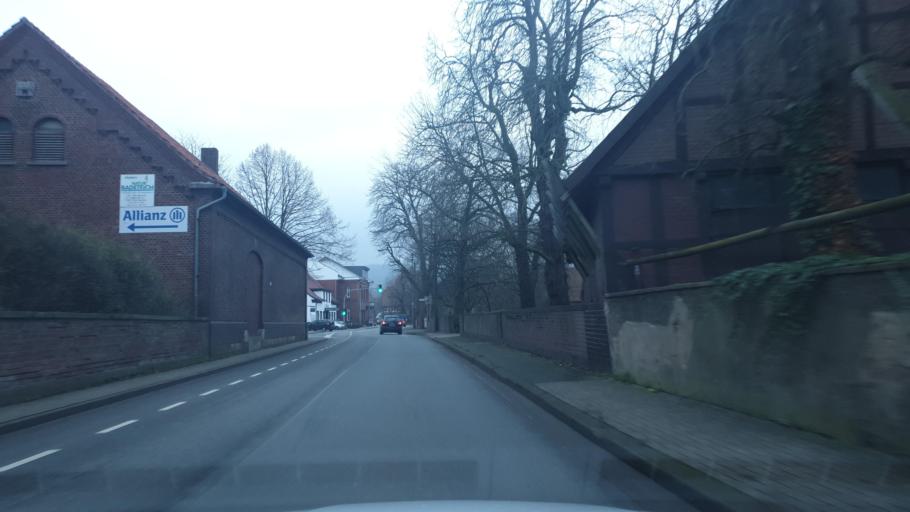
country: DE
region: North Rhine-Westphalia
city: Porta Westfalica
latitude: 52.2639
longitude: 8.9289
